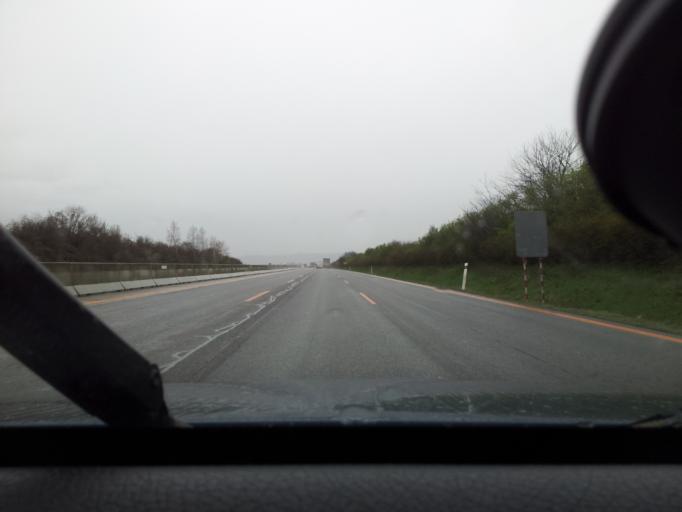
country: SK
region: Bratislavsky
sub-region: Okres Pezinok
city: Pezinok
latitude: 48.2149
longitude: 17.2824
